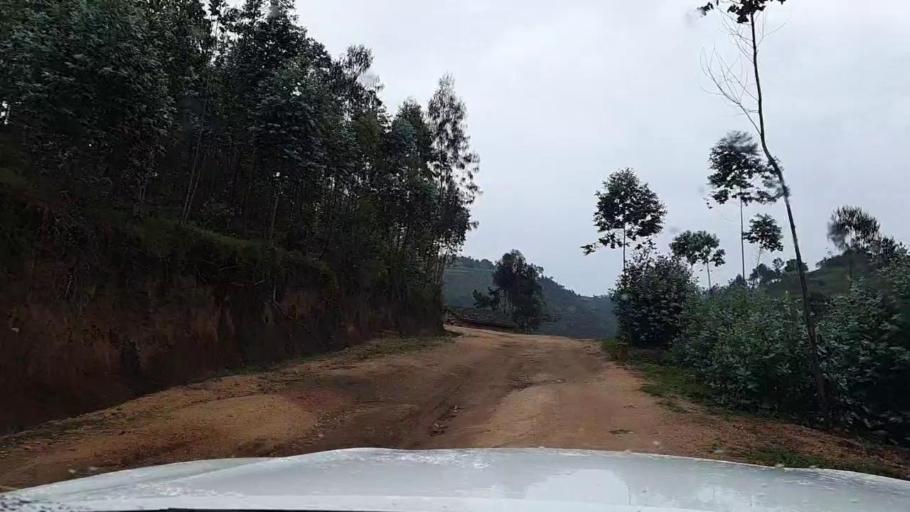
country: RW
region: Southern Province
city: Nzega
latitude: -2.4686
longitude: 29.5038
